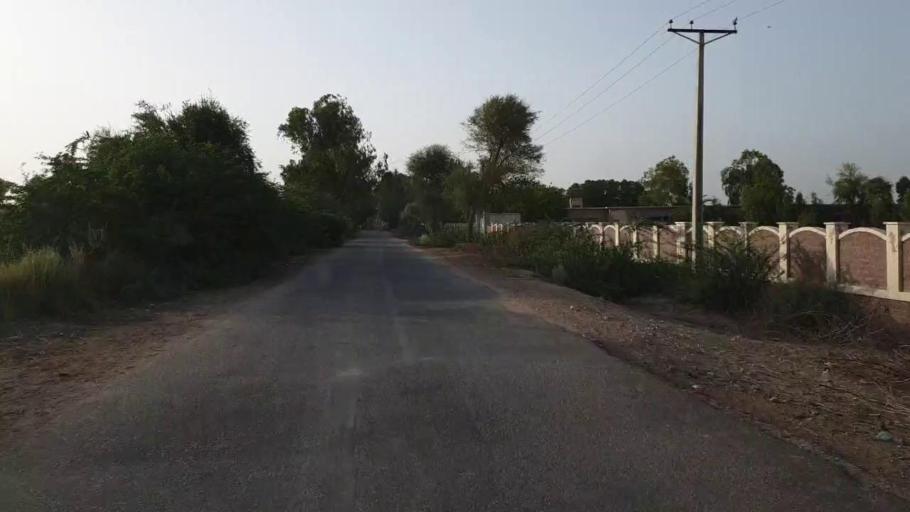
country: PK
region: Sindh
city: Bozdar
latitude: 27.1184
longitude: 68.9566
